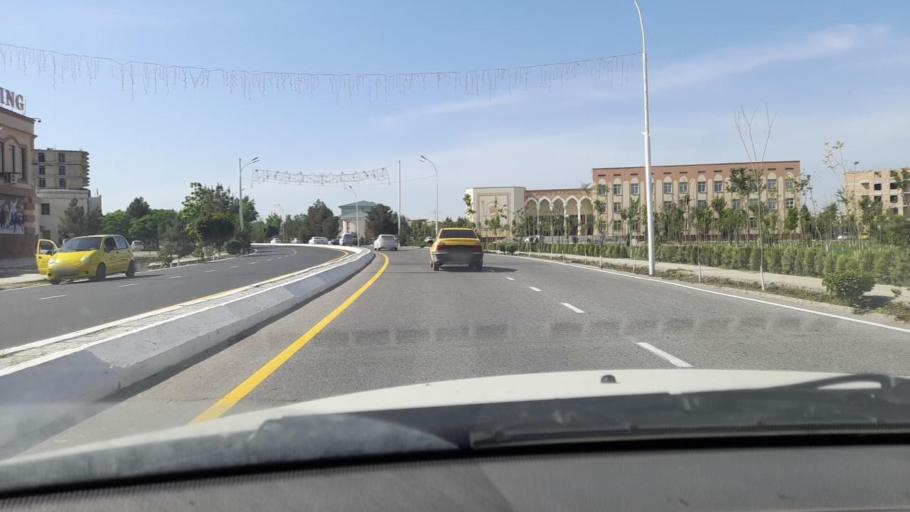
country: UZ
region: Bukhara
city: Bukhara
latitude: 39.7853
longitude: 64.4294
